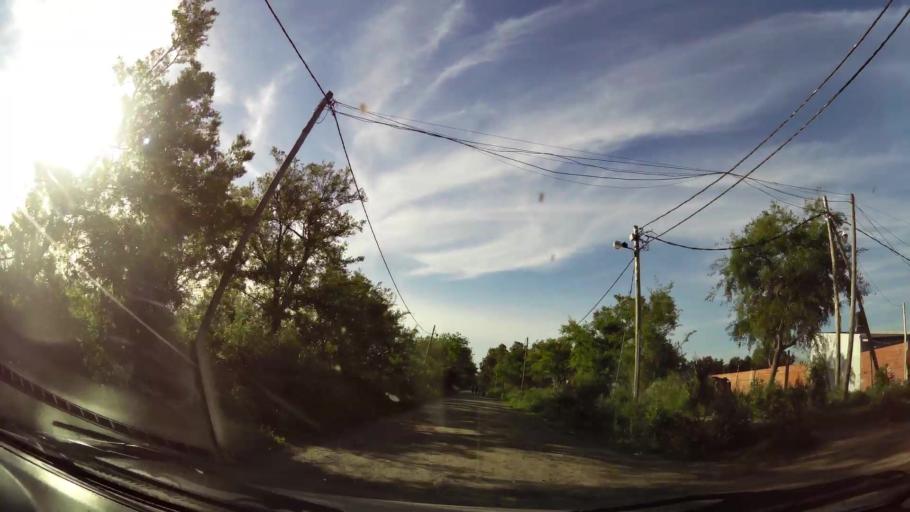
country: AR
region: Buenos Aires
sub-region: Partido de Almirante Brown
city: Adrogue
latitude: -34.8190
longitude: -58.3289
